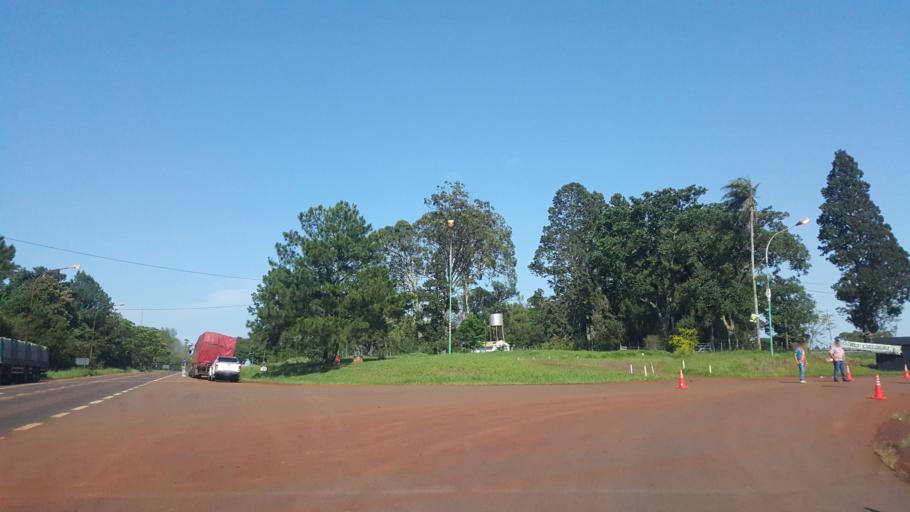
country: AR
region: Misiones
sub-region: Departamento de Apostoles
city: San Jose
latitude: -27.7878
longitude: -55.8306
